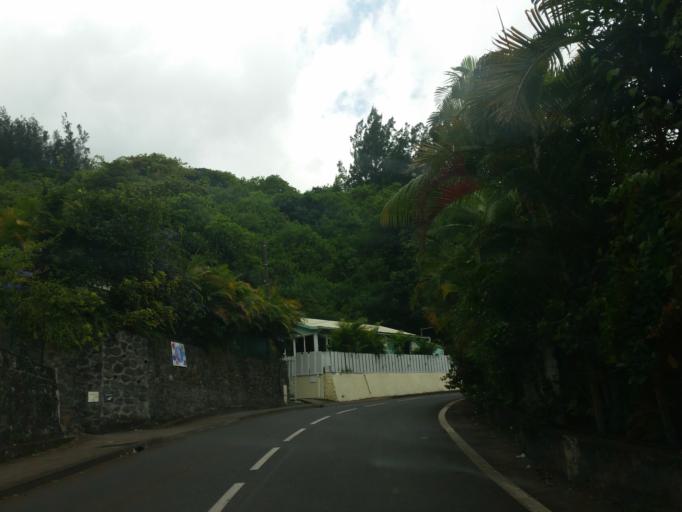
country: RE
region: Reunion
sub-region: Reunion
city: L'Entre-Deux
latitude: -21.2473
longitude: 55.4729
